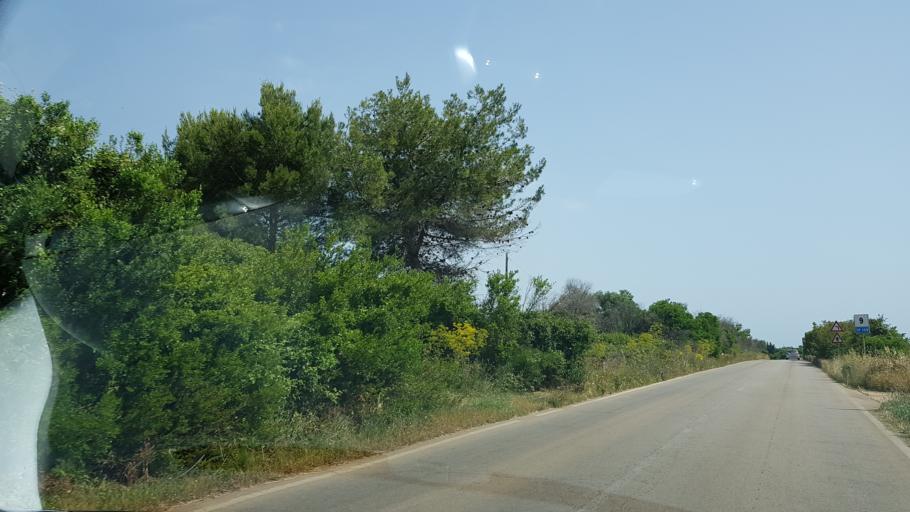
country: IT
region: Apulia
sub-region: Provincia di Lecce
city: Porto Cesareo
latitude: 40.3282
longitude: 17.8530
